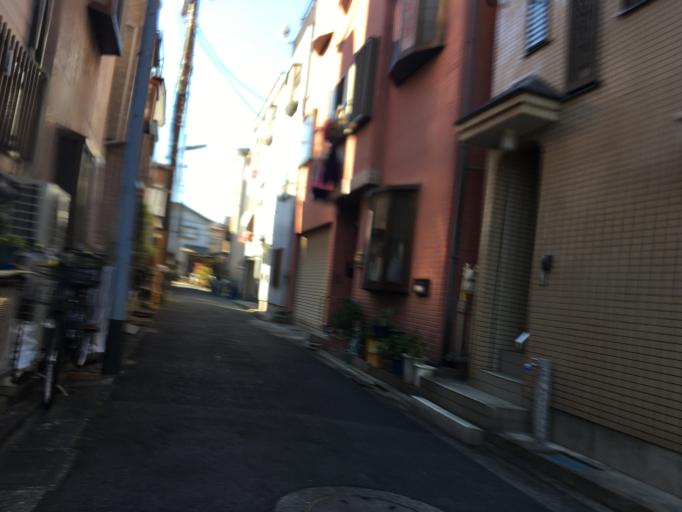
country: JP
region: Tokyo
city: Urayasu
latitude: 35.6917
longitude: 139.8917
